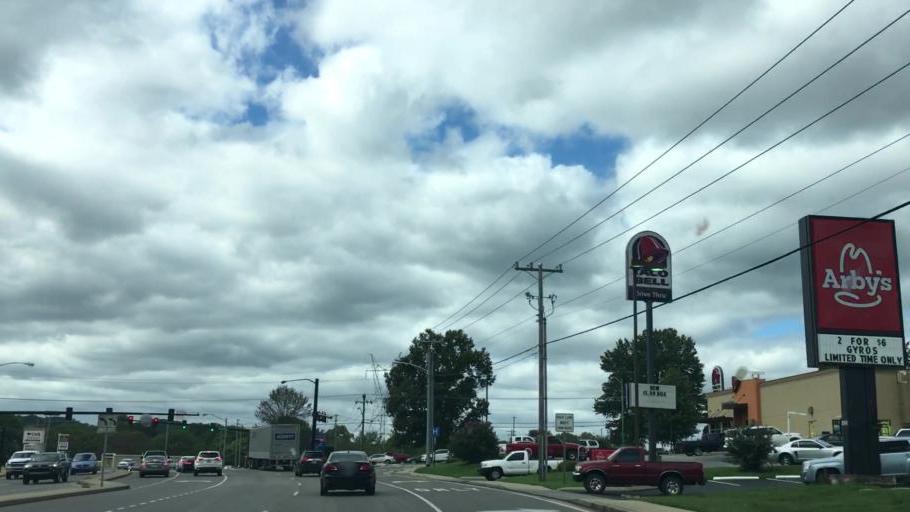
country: US
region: Tennessee
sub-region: Maury County
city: Columbia
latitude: 35.6041
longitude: -87.0665
